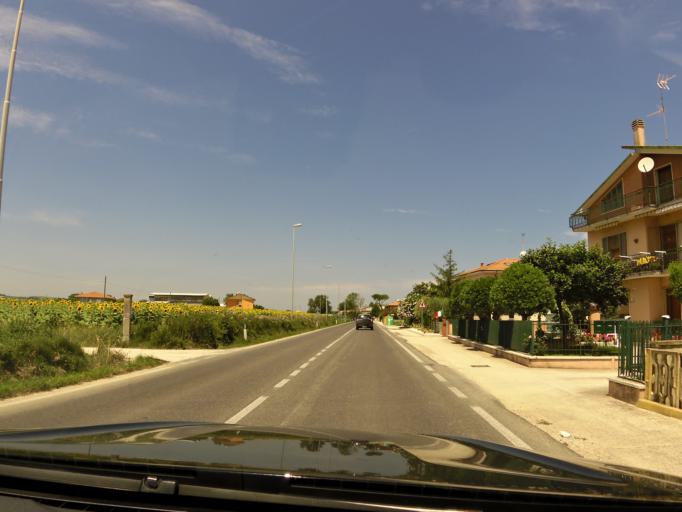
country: IT
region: The Marches
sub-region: Provincia di Pesaro e Urbino
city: Marotta
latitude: 43.7889
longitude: 13.1071
